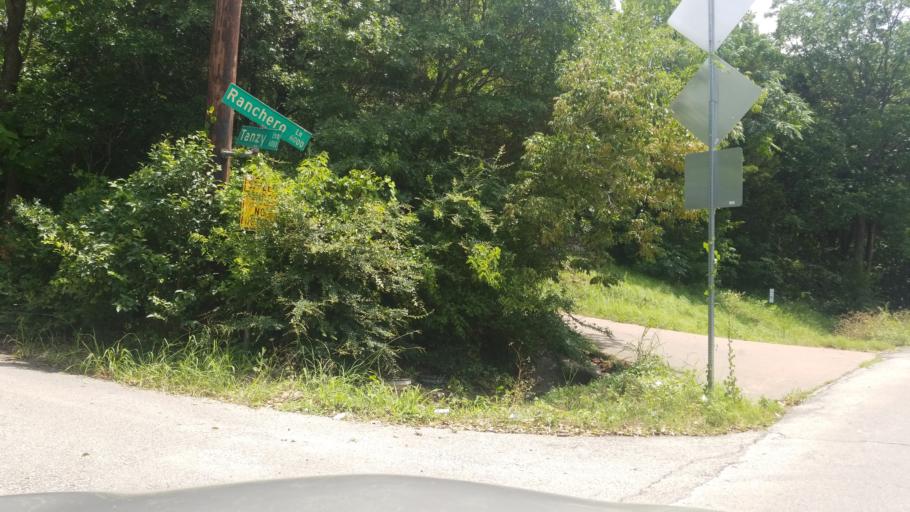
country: US
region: Texas
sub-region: Dallas County
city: Duncanville
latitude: 32.6801
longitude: -96.9246
